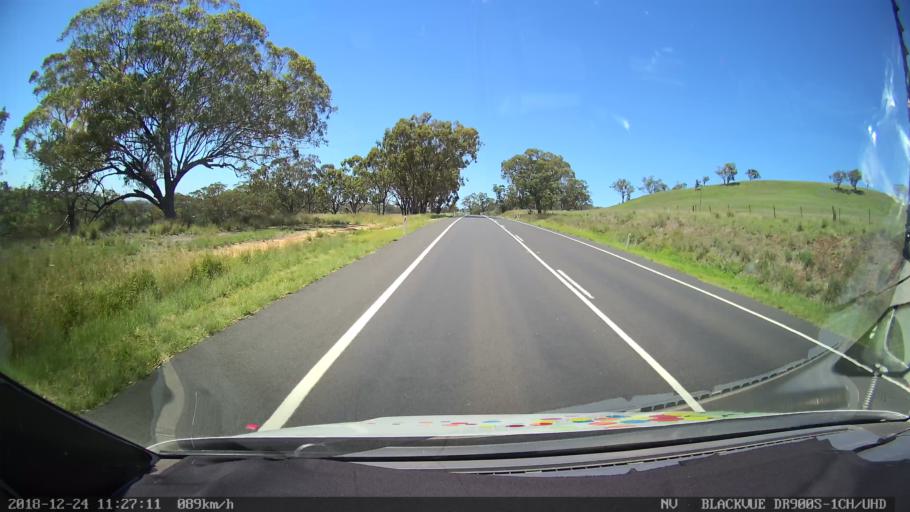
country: AU
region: New South Wales
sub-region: Upper Hunter Shire
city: Merriwa
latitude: -32.1788
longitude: 150.4342
